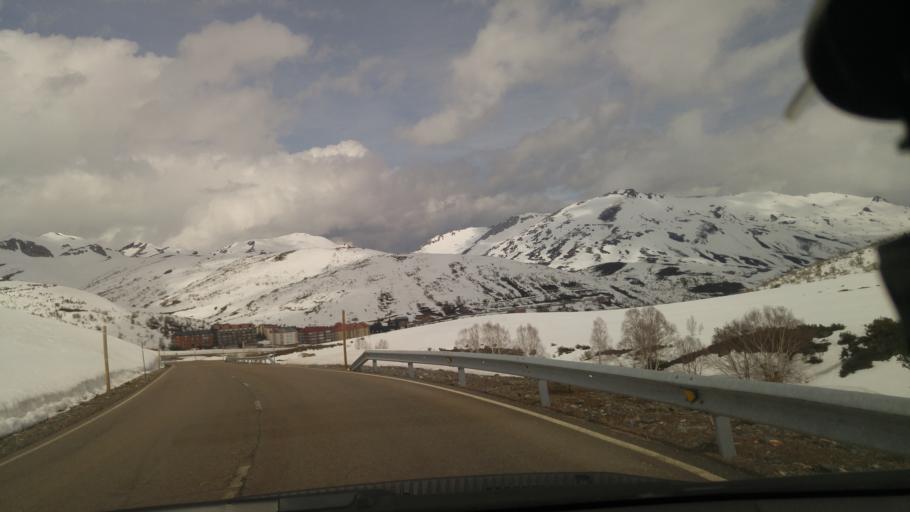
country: ES
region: Castille and Leon
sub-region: Provincia de Leon
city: Puebla de Lillo
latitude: 43.0584
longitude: -5.3745
